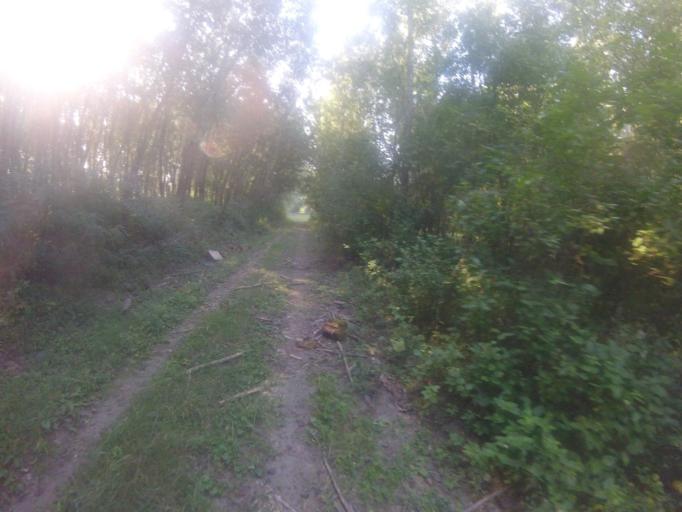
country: HU
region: Bacs-Kiskun
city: Baja
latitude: 46.1847
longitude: 18.9178
